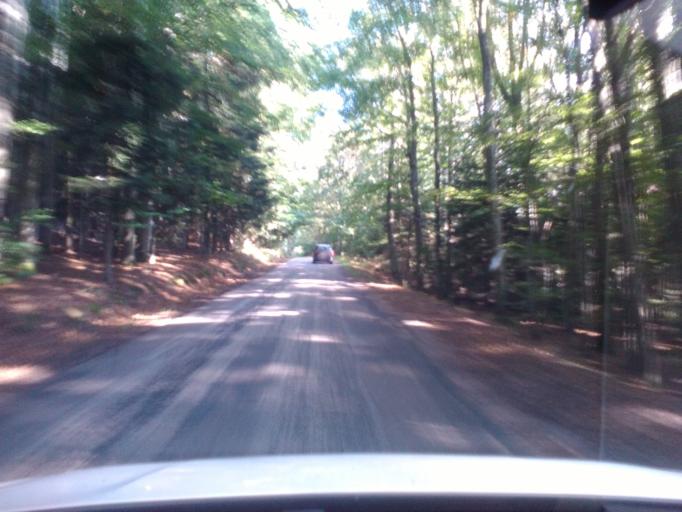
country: FR
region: Lorraine
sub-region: Departement des Vosges
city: Corcieux
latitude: 48.1603
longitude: 6.9044
